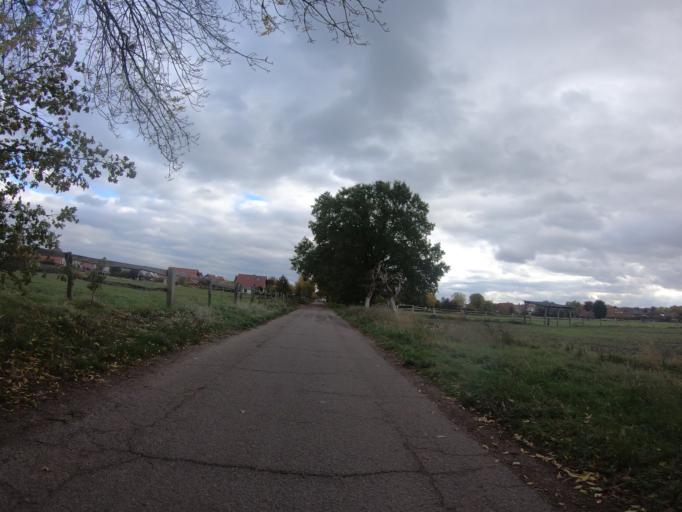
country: DE
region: Lower Saxony
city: Vordorf
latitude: 52.3673
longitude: 10.5143
